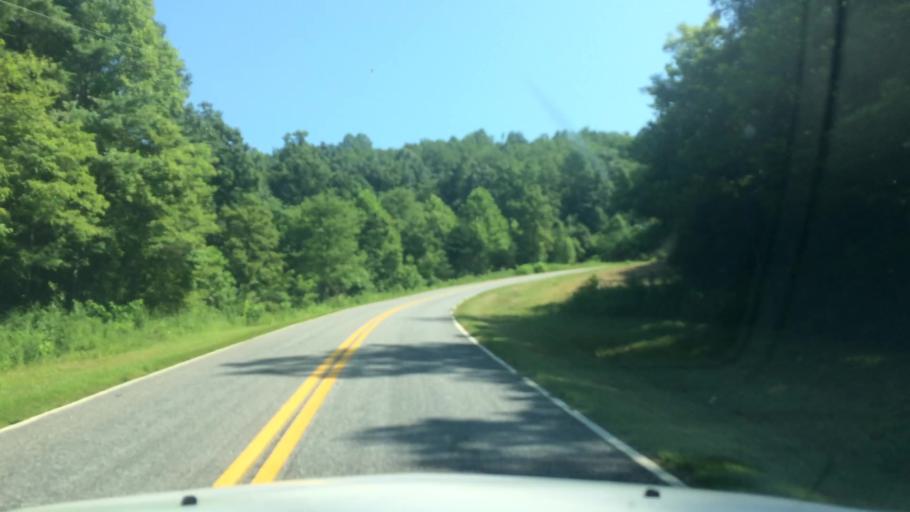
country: US
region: North Carolina
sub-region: Alexander County
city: Taylorsville
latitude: 35.9920
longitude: -81.2798
